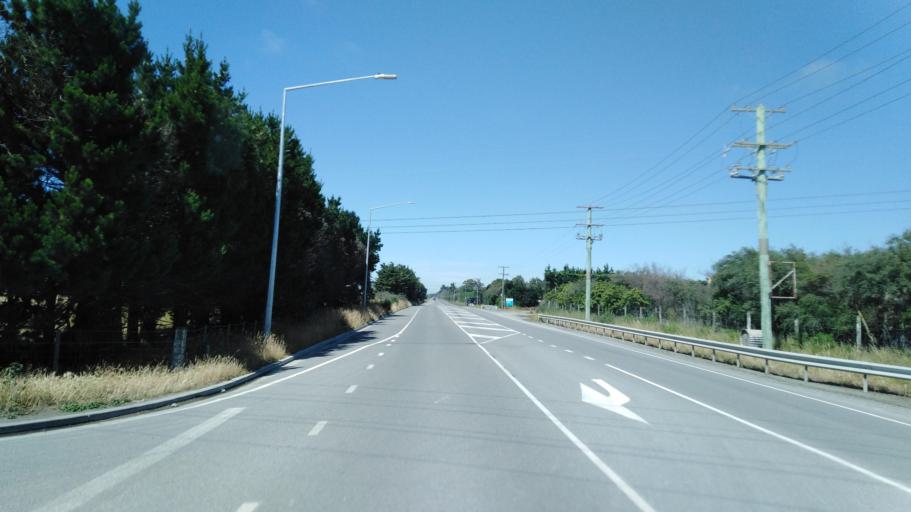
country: NZ
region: Canterbury
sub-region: Selwyn District
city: Prebbleton
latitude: -43.5277
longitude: 172.5001
